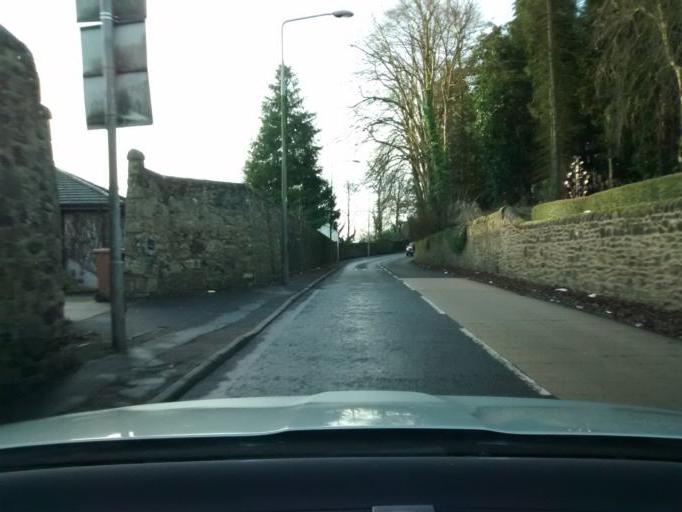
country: GB
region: Scotland
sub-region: West Lothian
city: Mid Calder
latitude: 55.8942
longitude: -3.4779
